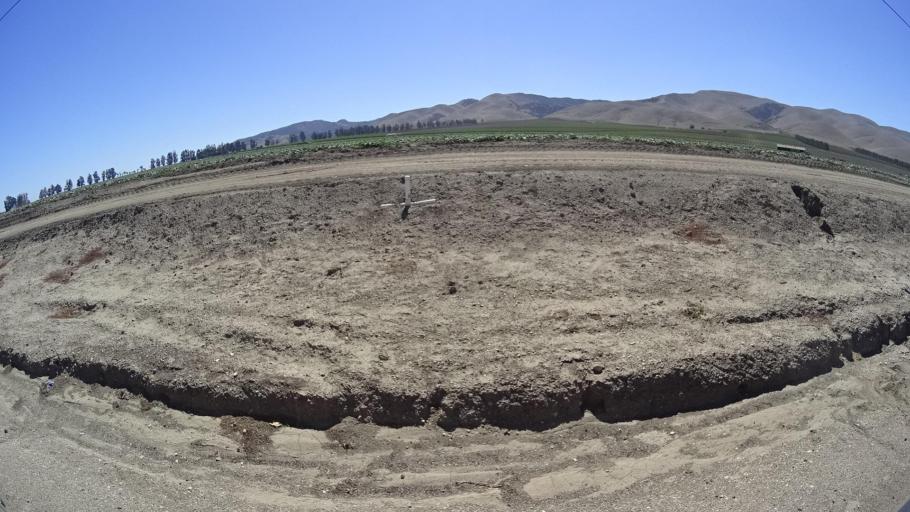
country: US
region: California
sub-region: Monterey County
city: Greenfield
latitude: 36.2864
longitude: -121.2400
